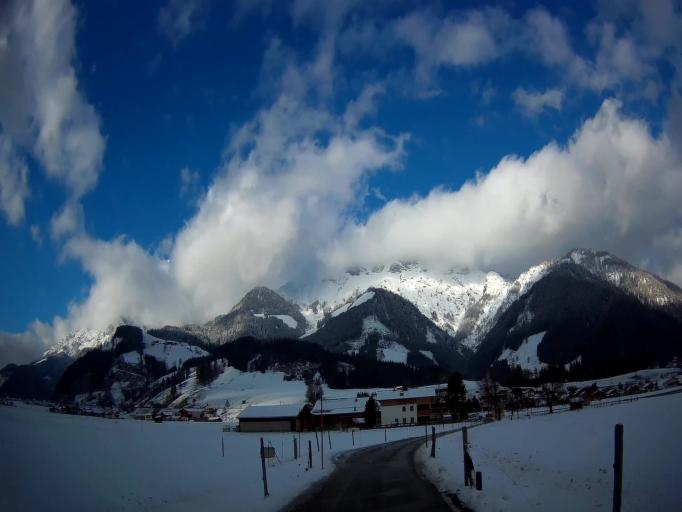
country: AT
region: Salzburg
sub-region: Politischer Bezirk Zell am See
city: Leogang
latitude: 47.4414
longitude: 12.7966
